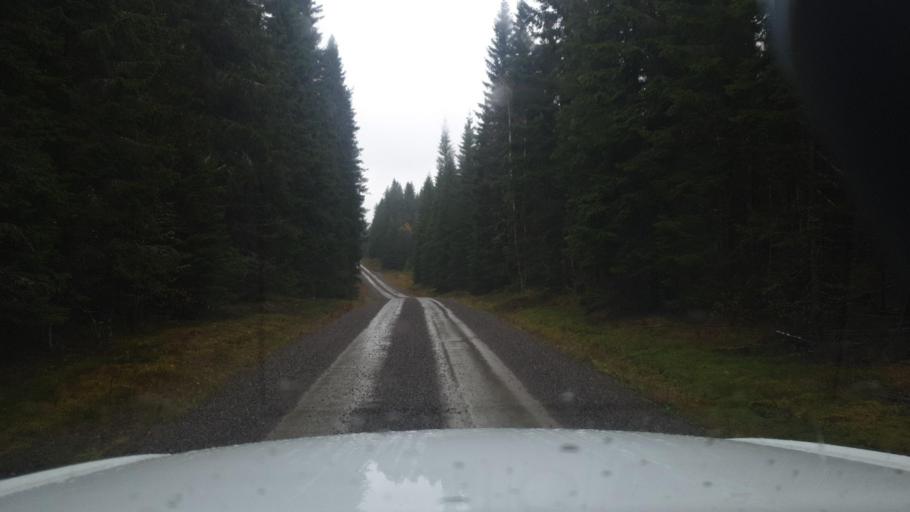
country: SE
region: Vaermland
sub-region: Eda Kommun
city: Charlottenberg
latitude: 60.0668
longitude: 12.6243
